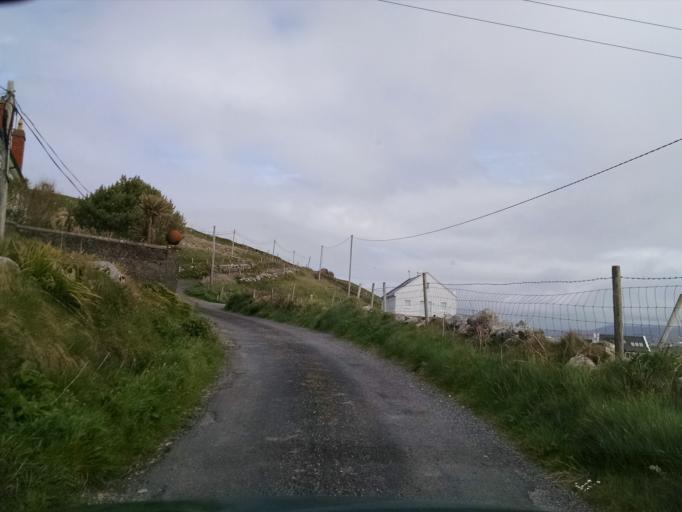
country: IE
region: Connaught
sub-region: County Galway
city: Clifden
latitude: 53.7640
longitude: -9.8775
